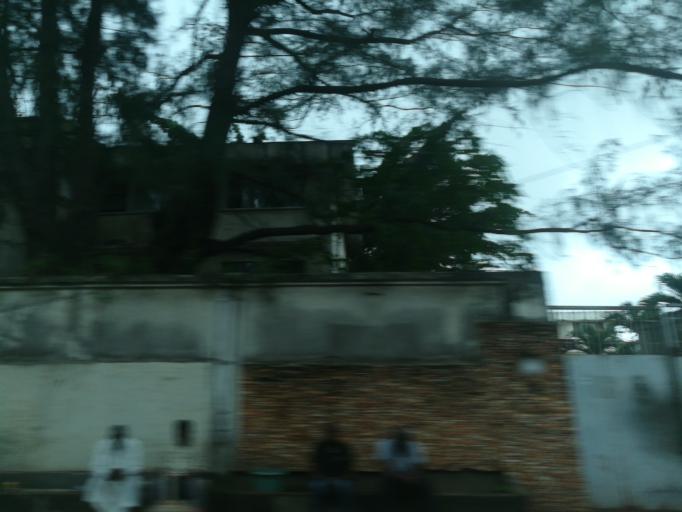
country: NG
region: Lagos
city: Ikoyi
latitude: 6.4239
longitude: 3.4226
